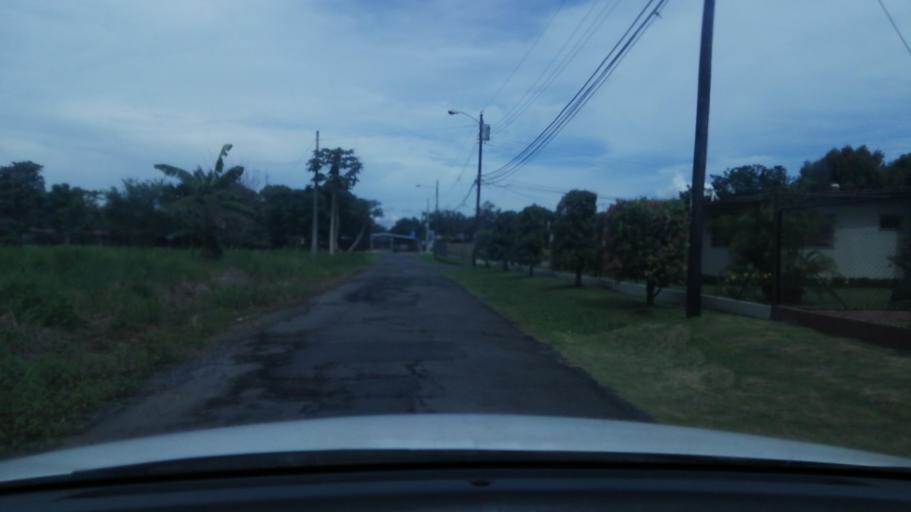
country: PA
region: Chiriqui
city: David
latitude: 8.4195
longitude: -82.4510
